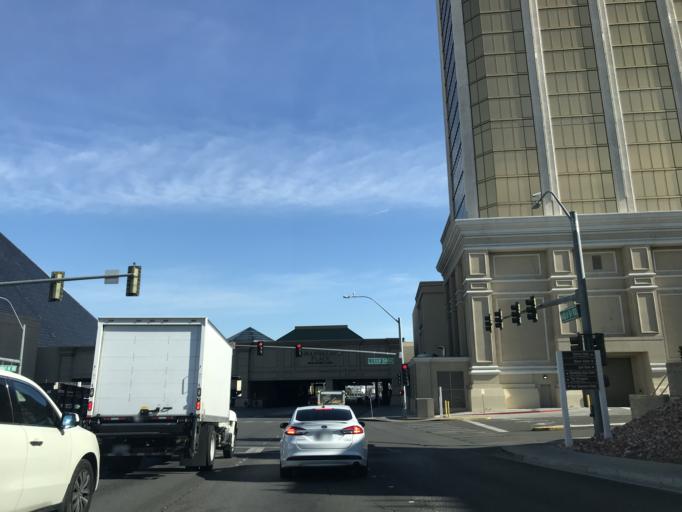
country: US
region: Nevada
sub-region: Clark County
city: Paradise
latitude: 36.0935
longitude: -115.1785
